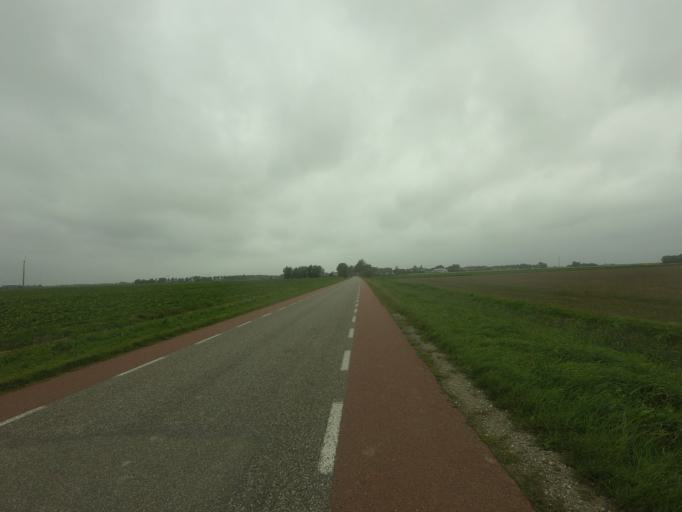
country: NL
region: Friesland
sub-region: Gemeente Ferwerderadiel
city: Ferwert
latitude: 53.3353
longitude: 5.8446
